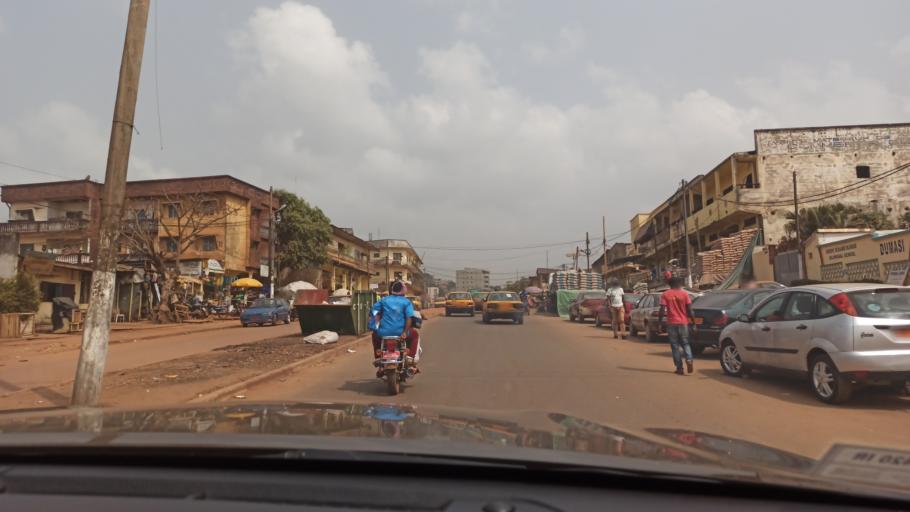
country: CM
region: Centre
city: Yaounde
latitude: 3.8840
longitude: 11.4920
